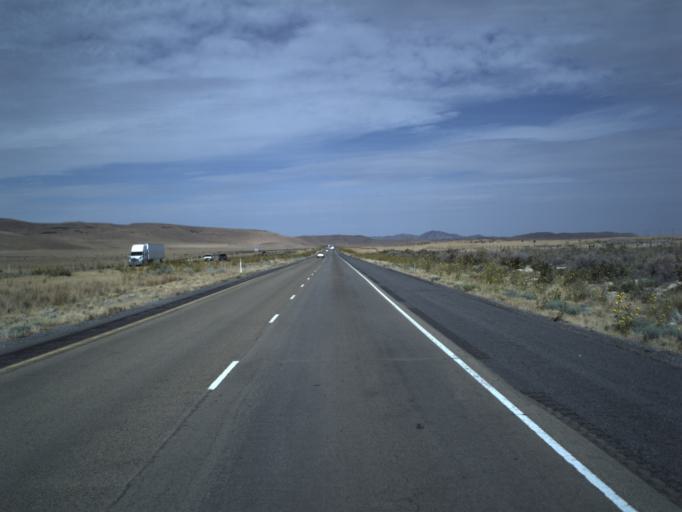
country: US
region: Utah
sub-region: Tooele County
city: Grantsville
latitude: 40.7877
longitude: -112.8265
